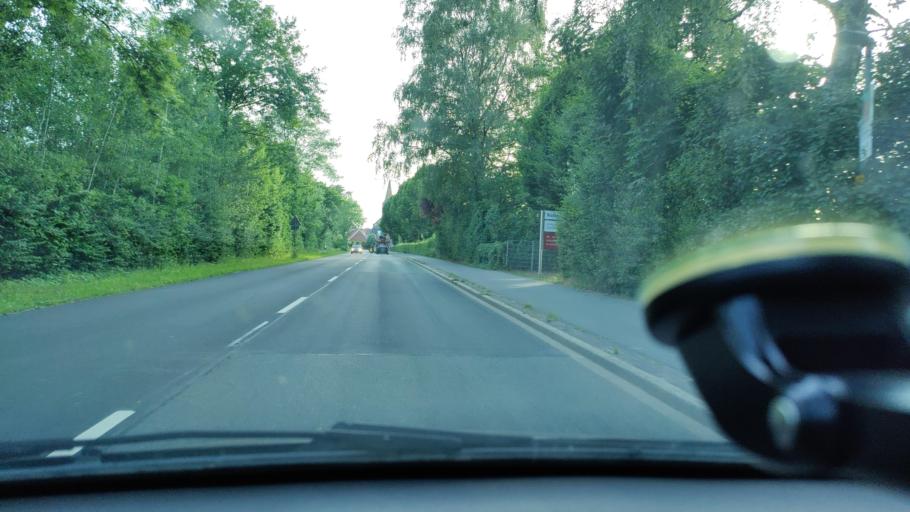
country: DE
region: North Rhine-Westphalia
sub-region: Regierungsbezirk Munster
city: Legden
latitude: 52.0075
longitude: 7.1385
